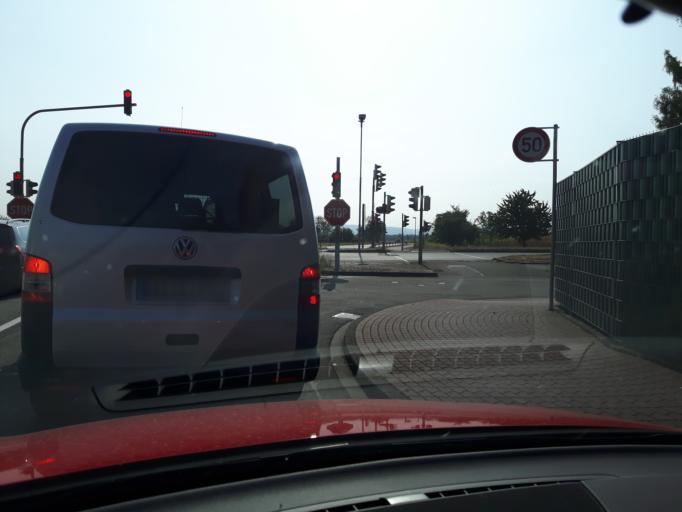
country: DE
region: Baden-Wuerttemberg
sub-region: Karlsruhe Region
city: Rheinstetten
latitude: 48.9742
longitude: 8.3172
